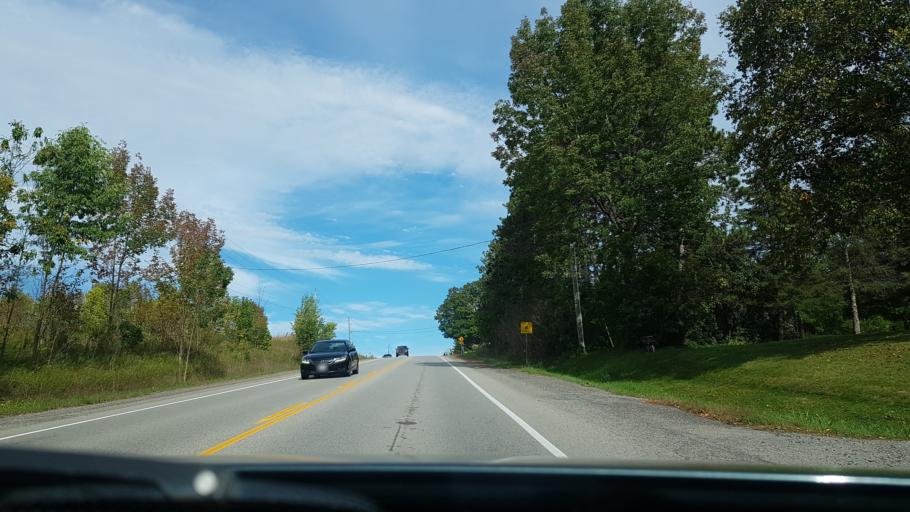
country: CA
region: Ontario
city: Angus
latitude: 44.4828
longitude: -79.8289
